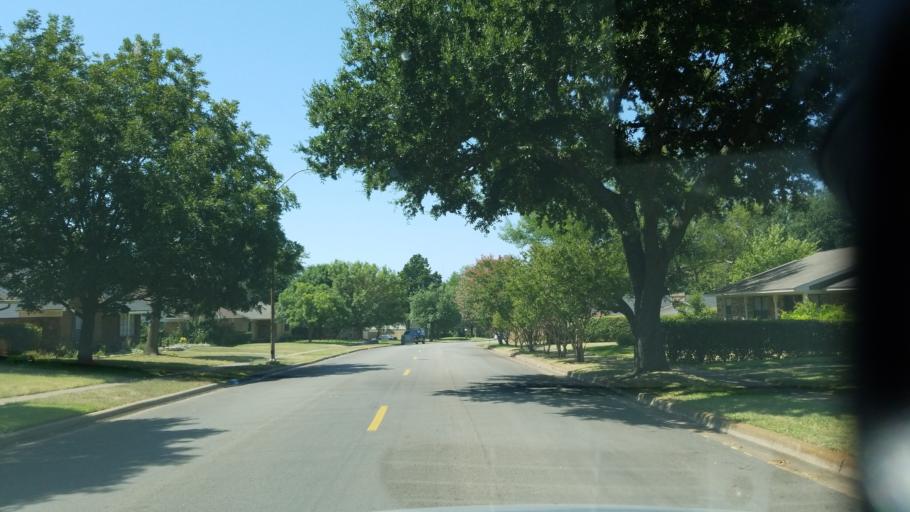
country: US
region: Texas
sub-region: Dallas County
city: Duncanville
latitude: 32.6518
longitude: -96.8972
